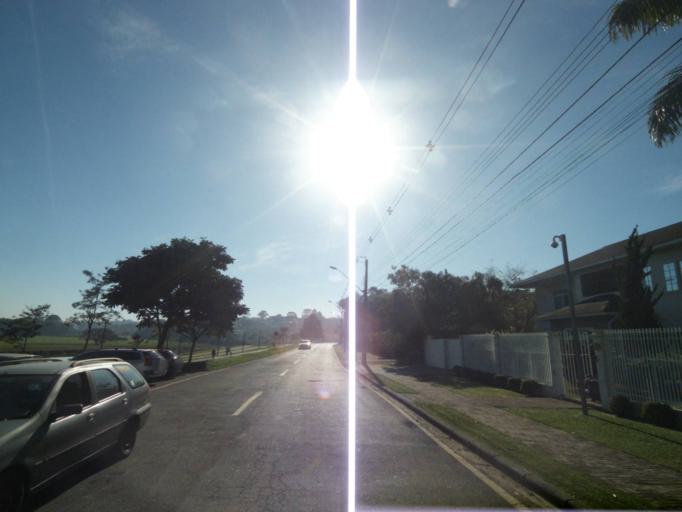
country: BR
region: Parana
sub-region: Curitiba
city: Curitiba
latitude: -25.4304
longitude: -49.3076
